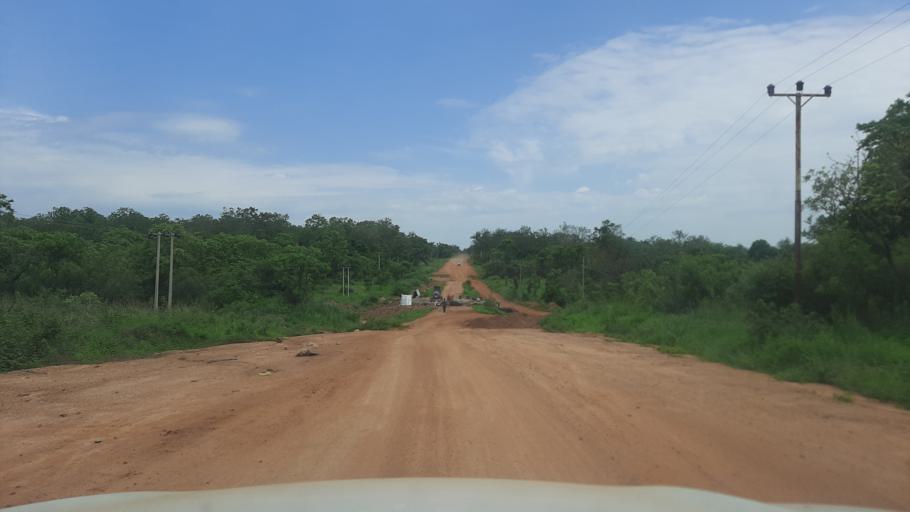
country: ET
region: Gambela
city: Gambela
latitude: 8.0899
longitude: 34.5895
